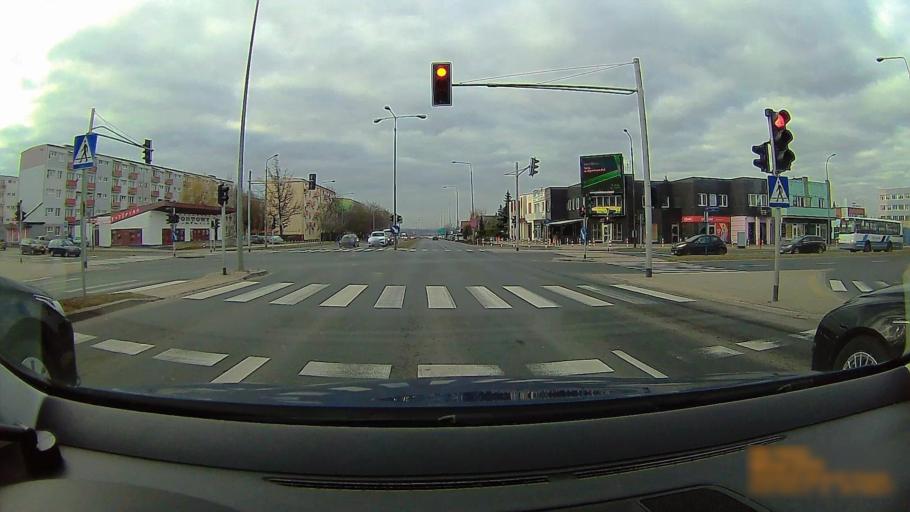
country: PL
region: Greater Poland Voivodeship
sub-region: Konin
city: Konin
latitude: 52.2297
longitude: 18.2450
